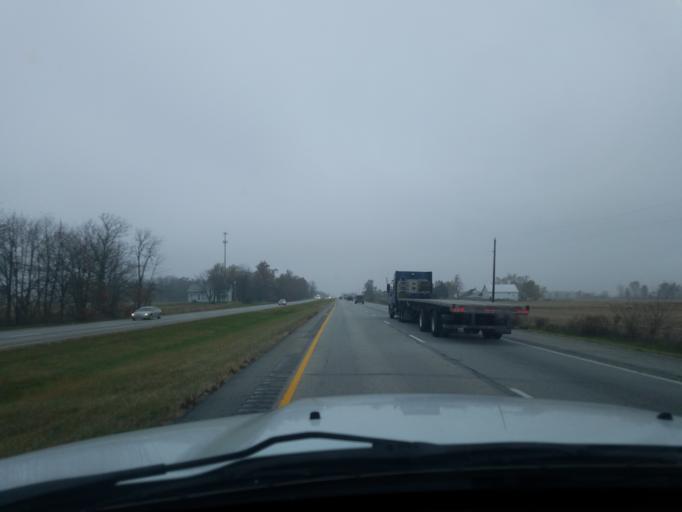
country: US
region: Indiana
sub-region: Hamilton County
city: Sheridan
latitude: 40.1485
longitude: -86.1278
